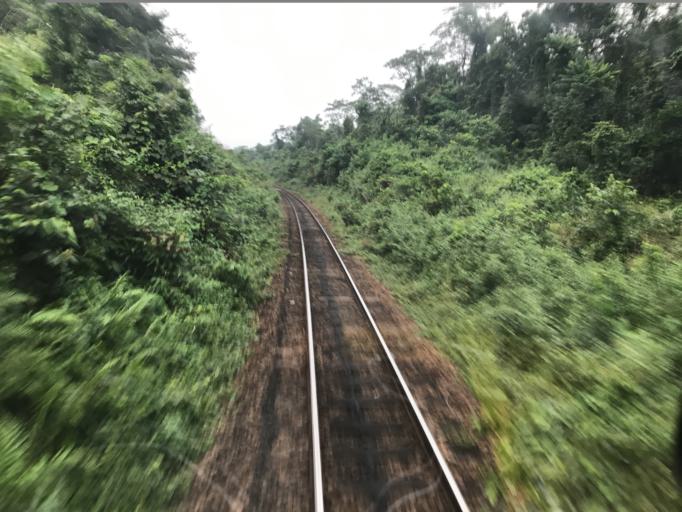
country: CM
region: Littoral
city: Edea
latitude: 3.9647
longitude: 10.0825
